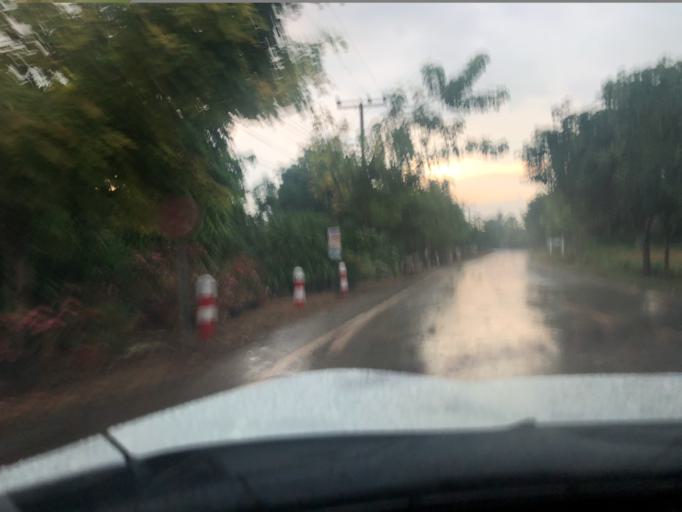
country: TH
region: Lop Buri
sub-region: Amphoe Tha Luang
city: Tha Luang
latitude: 15.0452
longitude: 101.2360
